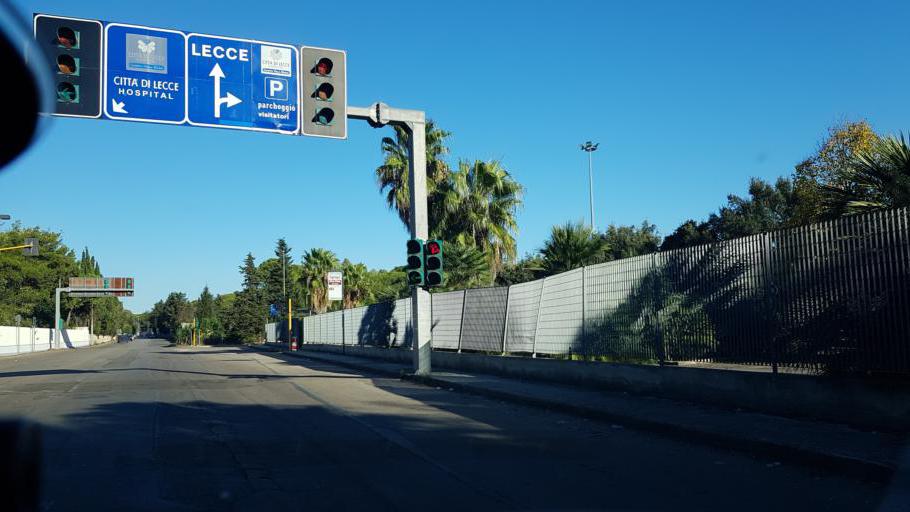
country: IT
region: Apulia
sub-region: Provincia di Lecce
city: San Pietro in Lama
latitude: 40.3392
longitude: 18.1292
